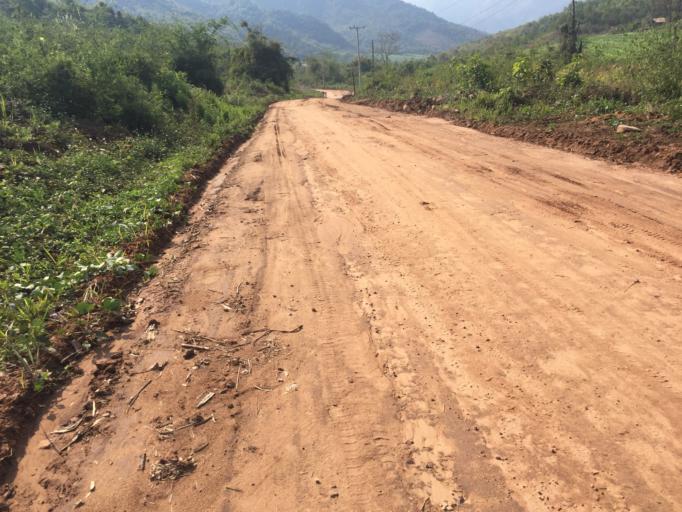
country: LA
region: Oudomxai
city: Muang La
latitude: 20.7448
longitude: 102.1311
